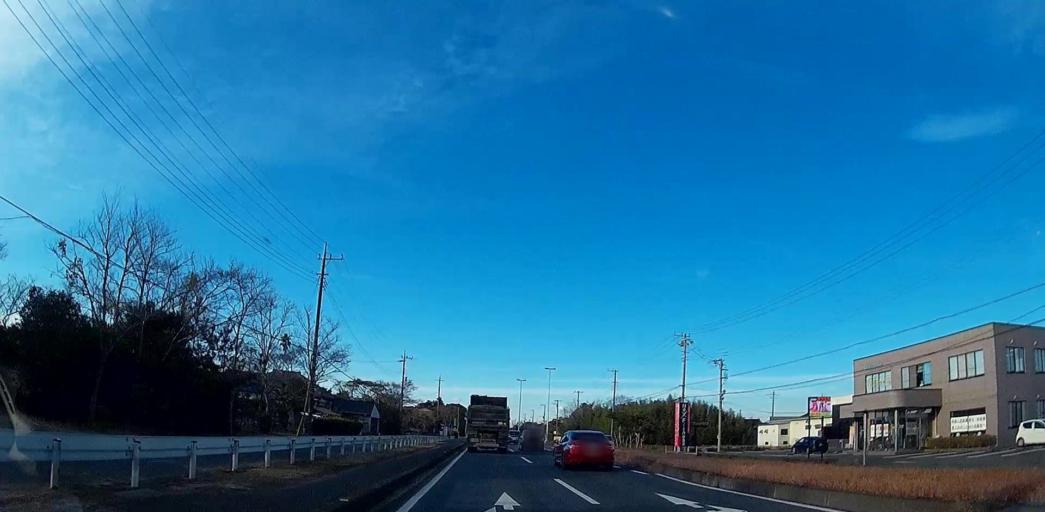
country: JP
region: Chiba
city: Omigawa
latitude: 35.8312
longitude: 140.7205
